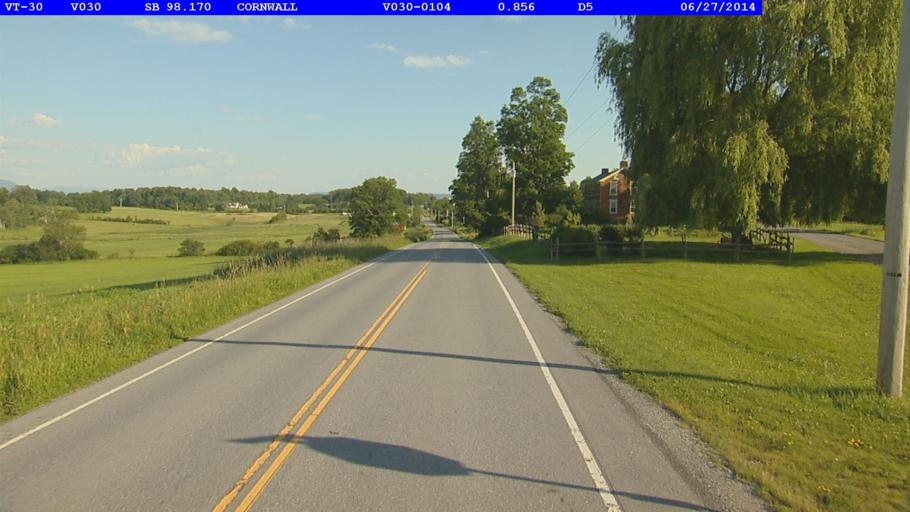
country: US
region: Vermont
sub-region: Addison County
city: Middlebury (village)
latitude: 43.9201
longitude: -73.2111
